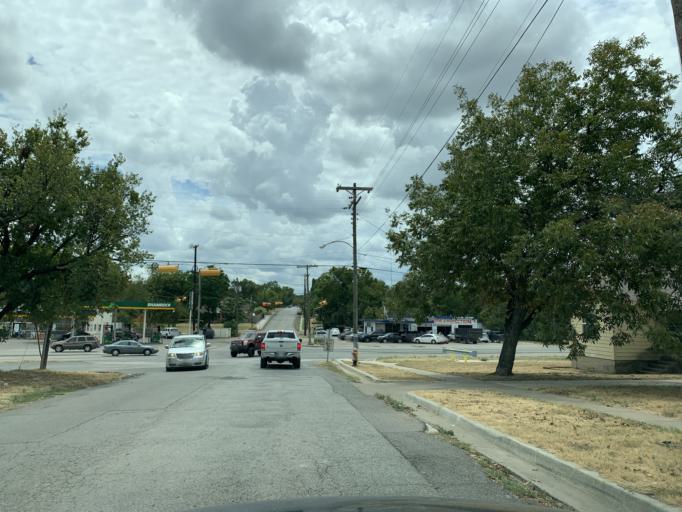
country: US
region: Texas
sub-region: Dallas County
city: Cockrell Hill
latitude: 32.7404
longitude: -96.8810
